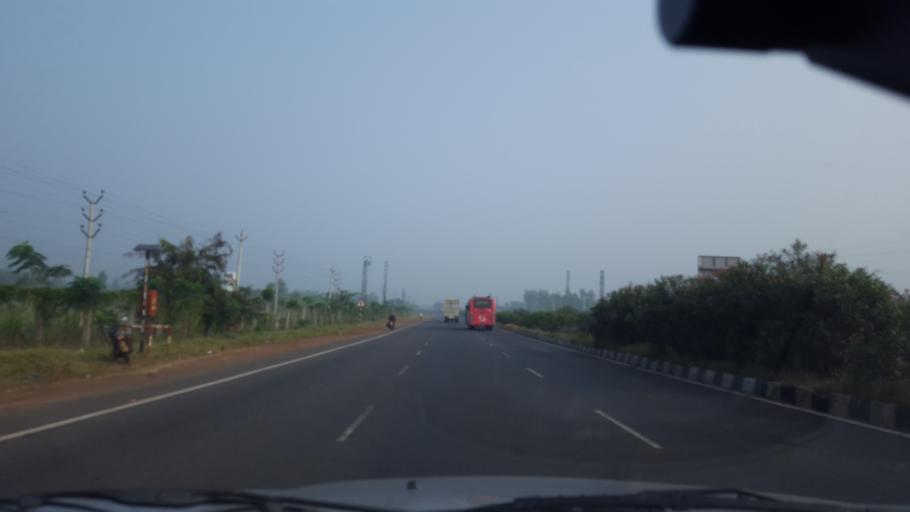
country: IN
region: Andhra Pradesh
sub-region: Prakasam
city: Singarayakonda
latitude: 15.3678
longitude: 80.0418
